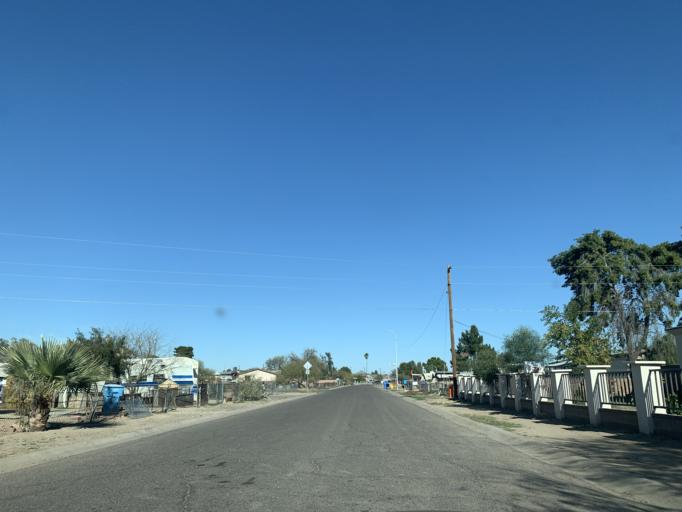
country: US
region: Arizona
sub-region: Maricopa County
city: Laveen
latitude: 33.3930
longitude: -112.1383
